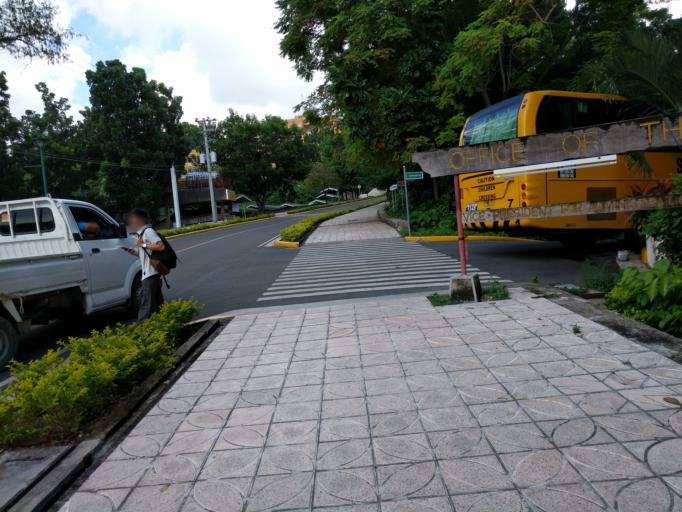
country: PH
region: Central Visayas
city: Mandaue City
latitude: 10.3545
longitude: 123.9121
